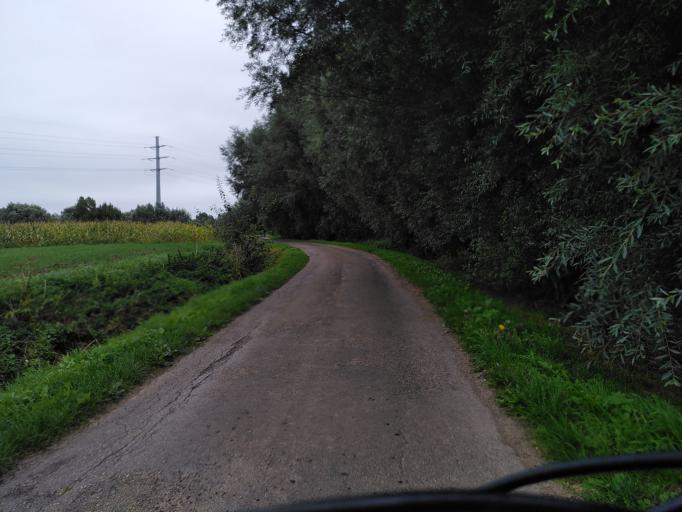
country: FR
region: Nord-Pas-de-Calais
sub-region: Departement du Pas-de-Calais
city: Guarbecque
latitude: 50.6244
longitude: 2.4922
